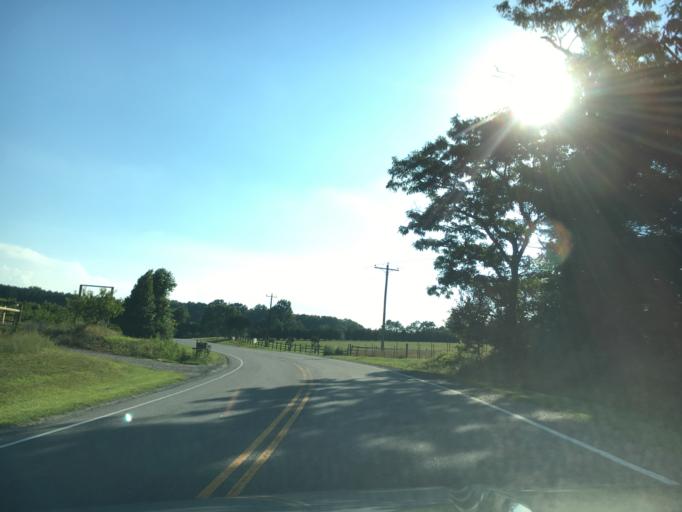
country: US
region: Virginia
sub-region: City of Bedford
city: Bedford
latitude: 37.2242
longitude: -79.5000
